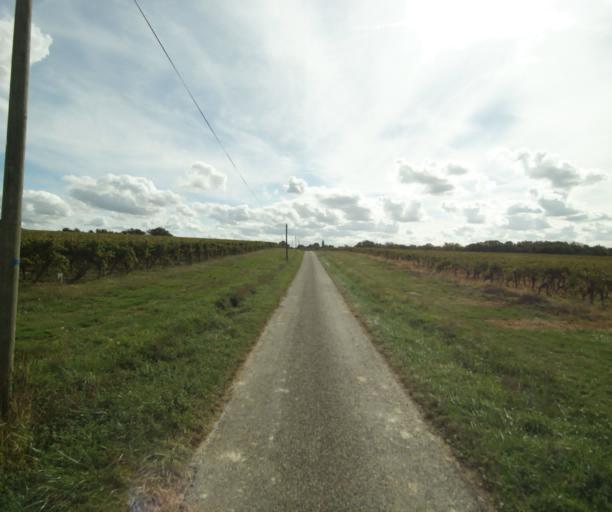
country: FR
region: Midi-Pyrenees
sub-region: Departement du Gers
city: Eauze
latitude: 43.8496
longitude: 0.1536
